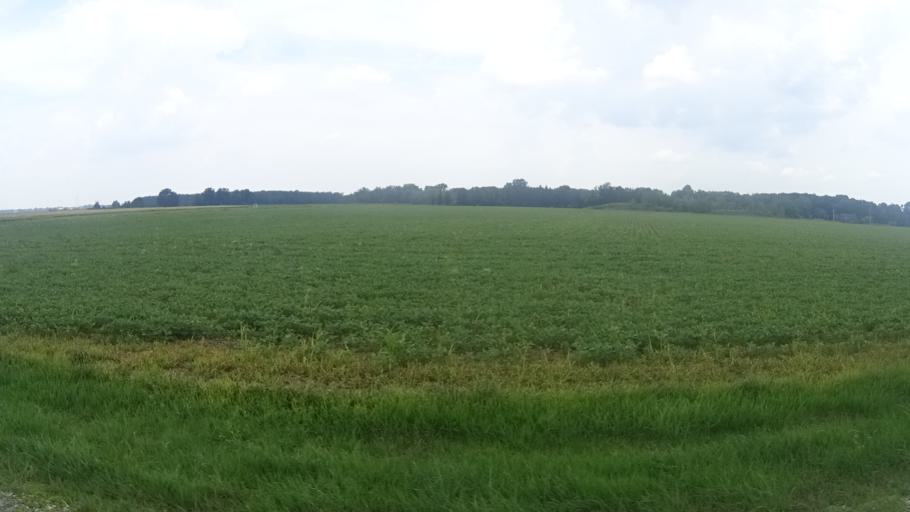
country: US
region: Ohio
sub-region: Erie County
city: Milan
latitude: 41.2936
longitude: -82.6609
